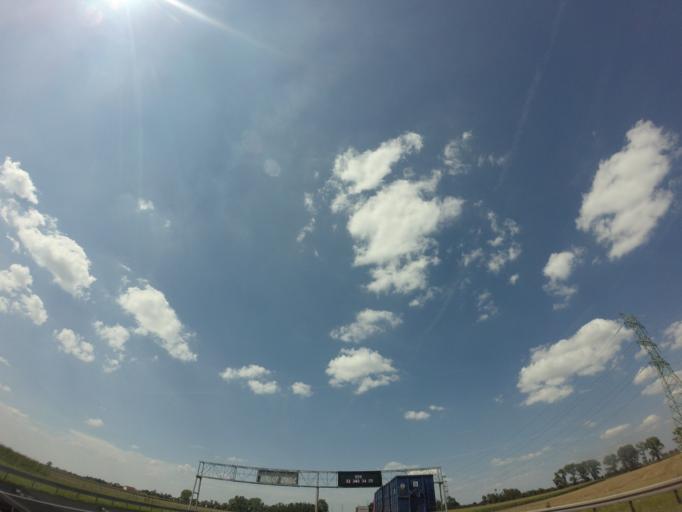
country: PL
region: Lower Silesian Voivodeship
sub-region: Powiat olawski
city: Wierzbno
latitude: 50.8861
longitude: 17.1930
